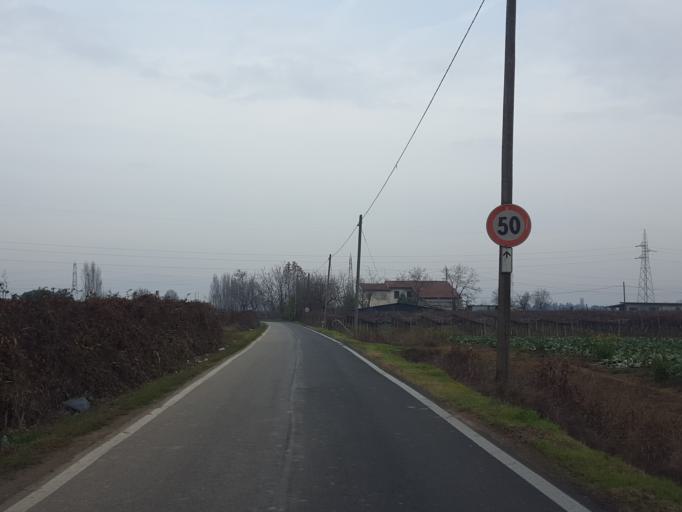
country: IT
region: Veneto
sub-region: Provincia di Verona
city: San Bonifacio
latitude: 45.3811
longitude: 11.2884
